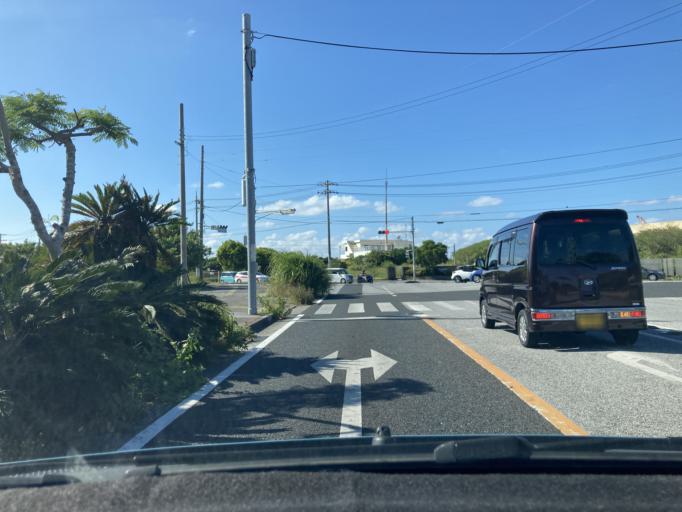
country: JP
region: Okinawa
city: Naha-shi
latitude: 26.2457
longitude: 127.6870
